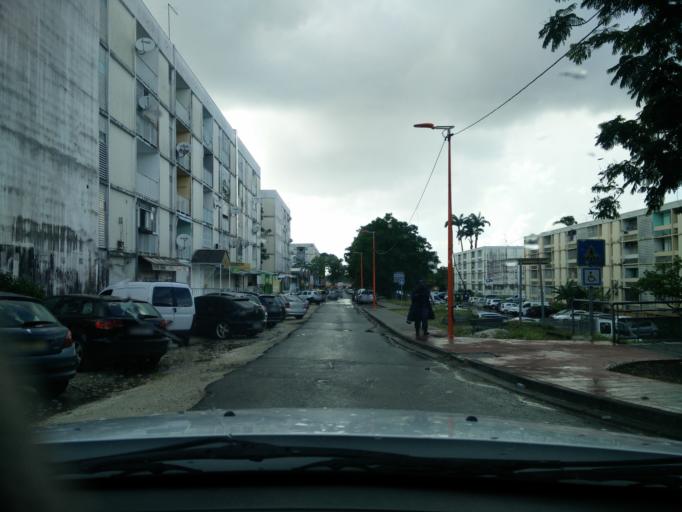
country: GP
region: Guadeloupe
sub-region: Guadeloupe
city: Pointe-a-Pitre
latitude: 16.2514
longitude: -61.5378
